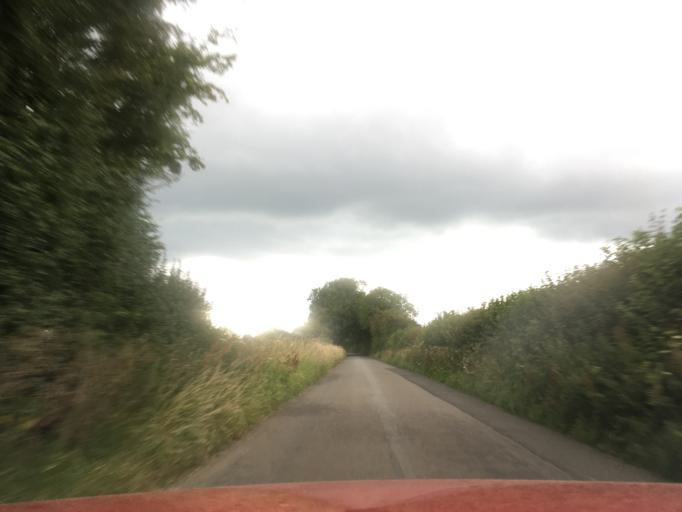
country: GB
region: England
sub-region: Gloucestershire
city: Shurdington
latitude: 51.7962
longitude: -2.1226
